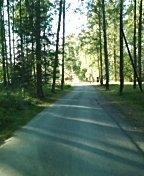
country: SE
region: Uppsala
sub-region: Habo Kommun
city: Balsta
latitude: 59.7053
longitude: 17.5401
